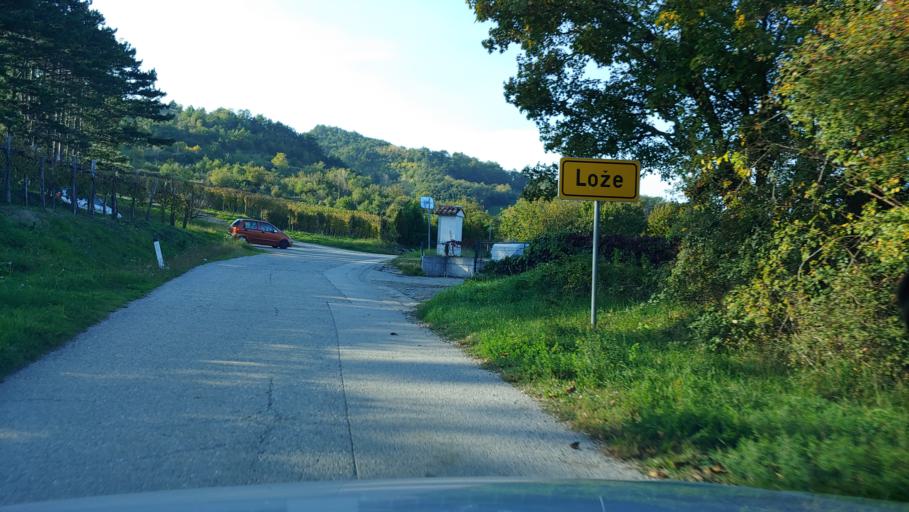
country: SI
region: Vipava
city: Vipava
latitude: 45.8240
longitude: 13.9392
